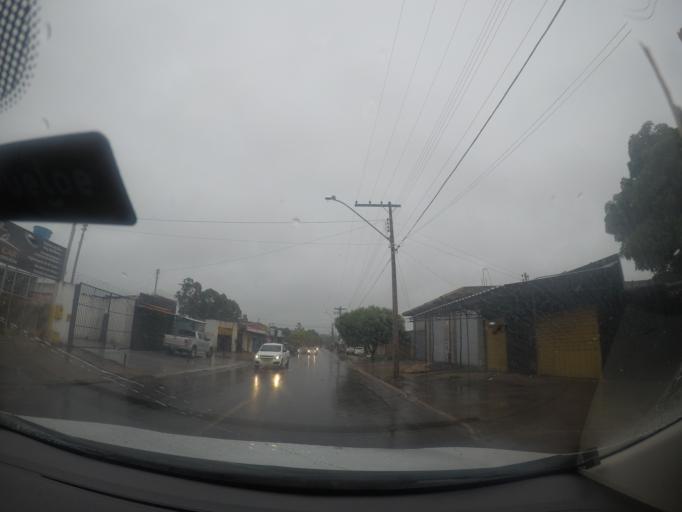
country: BR
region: Goias
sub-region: Goiania
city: Goiania
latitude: -16.6079
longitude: -49.3475
